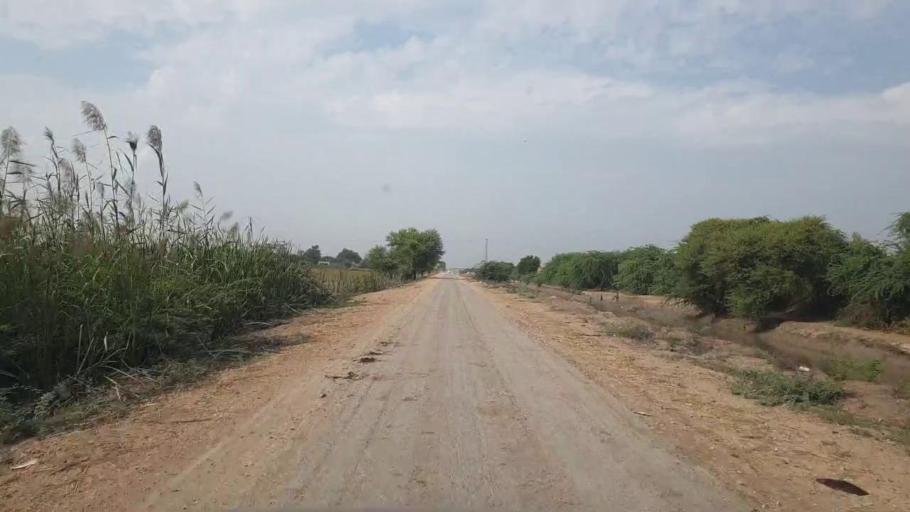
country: PK
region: Sindh
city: Kario
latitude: 24.6320
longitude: 68.5705
